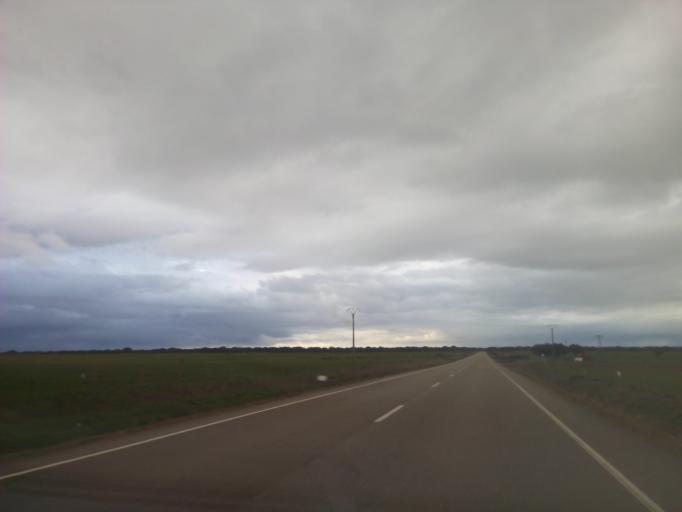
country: ES
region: Castille and Leon
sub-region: Provincia de Salamanca
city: Tamames
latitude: 40.6710
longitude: -6.1200
